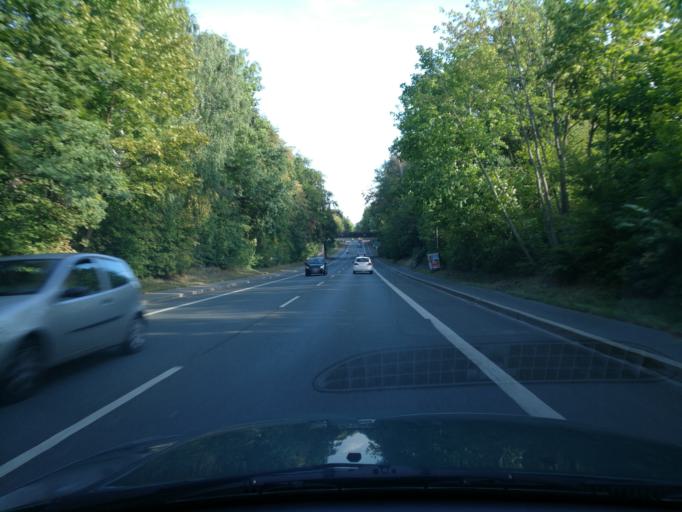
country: DE
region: Bavaria
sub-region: Regierungsbezirk Mittelfranken
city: Furth
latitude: 49.5029
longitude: 10.9810
